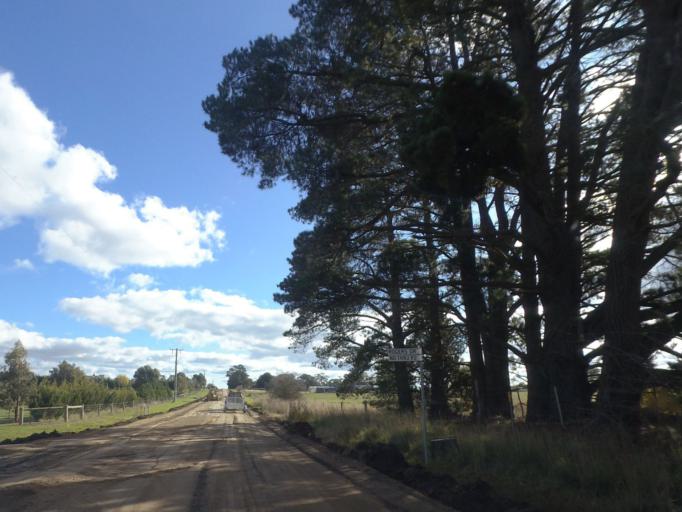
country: AU
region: Victoria
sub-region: Mount Alexander
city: Castlemaine
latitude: -37.2555
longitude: 144.4368
